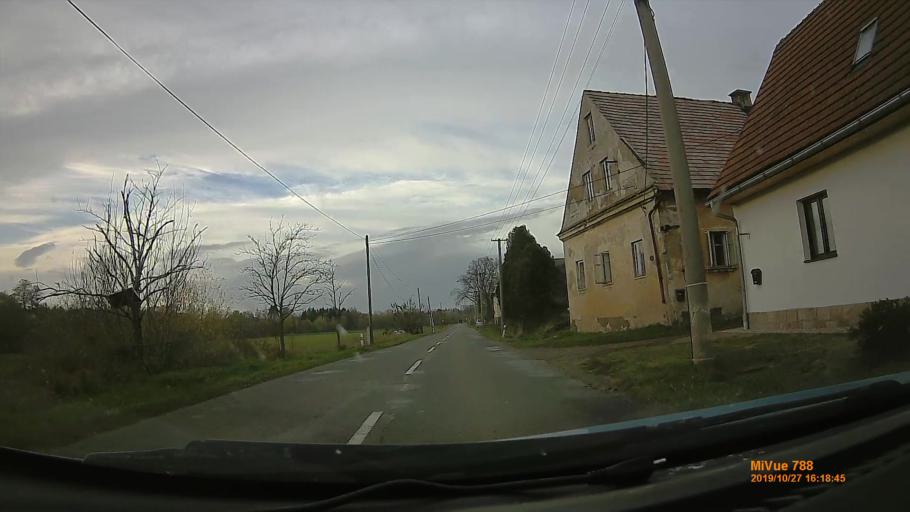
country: CZ
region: Kralovehradecky
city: Broumov
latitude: 50.5685
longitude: 16.3499
